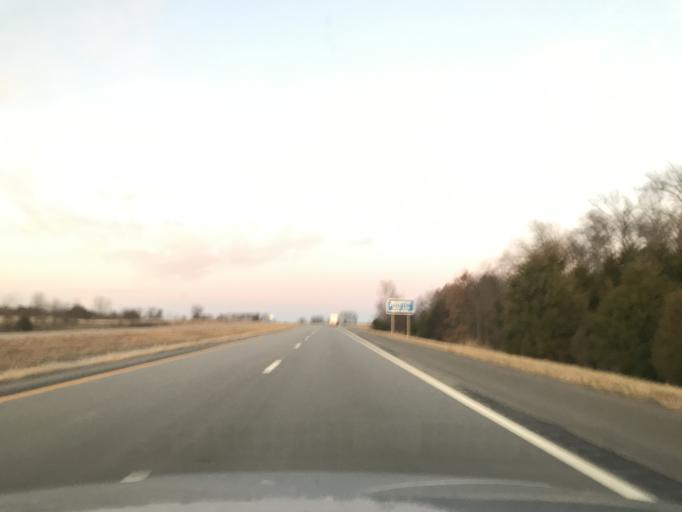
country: US
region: Missouri
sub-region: Marion County
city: Hannibal
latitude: 39.7107
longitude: -91.4565
